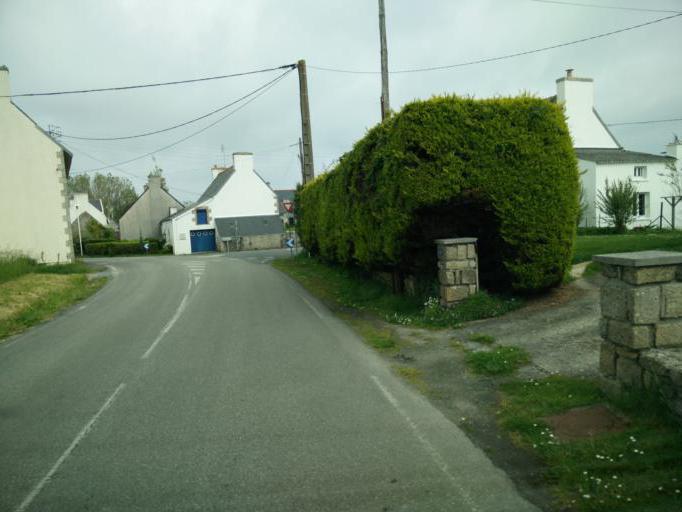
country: FR
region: Brittany
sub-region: Departement du Finistere
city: Plobannalec-Lesconil
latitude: 47.8025
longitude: -4.1910
